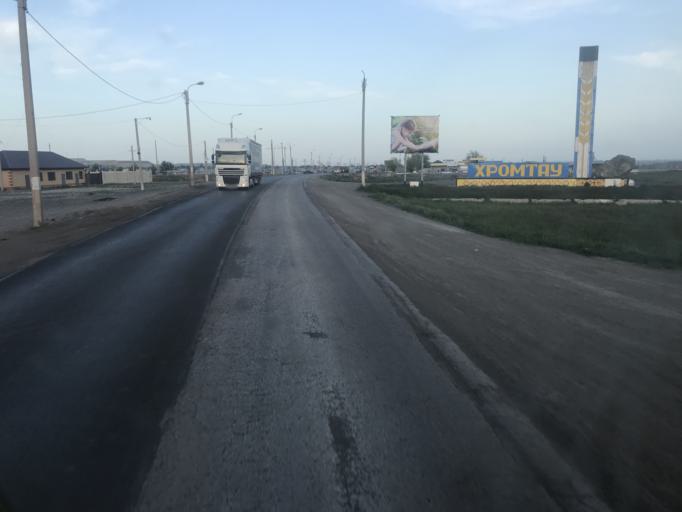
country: KZ
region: Aqtoebe
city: Khromtau
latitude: 50.2583
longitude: 58.4100
